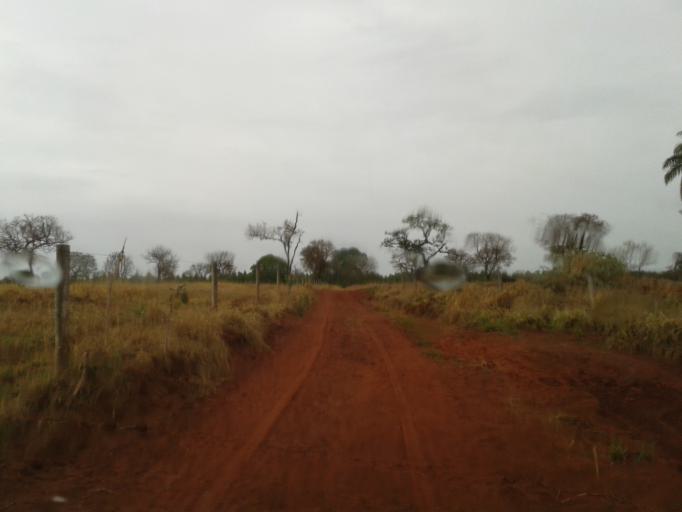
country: BR
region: Minas Gerais
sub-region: Campina Verde
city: Campina Verde
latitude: -19.3473
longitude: -49.5507
